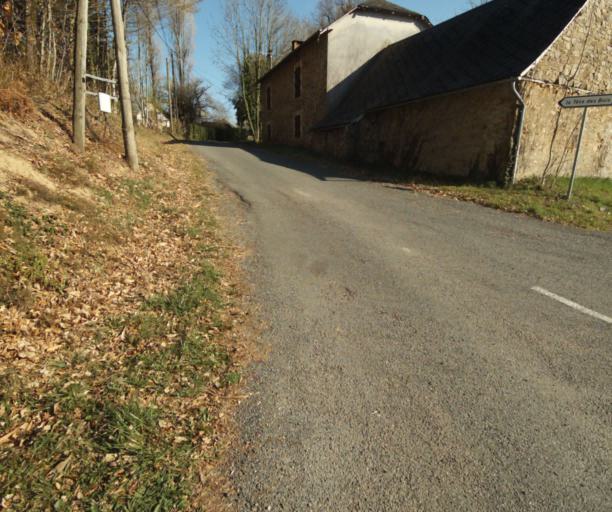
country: FR
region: Limousin
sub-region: Departement de la Correze
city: Saint-Clement
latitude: 45.3213
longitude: 1.6787
